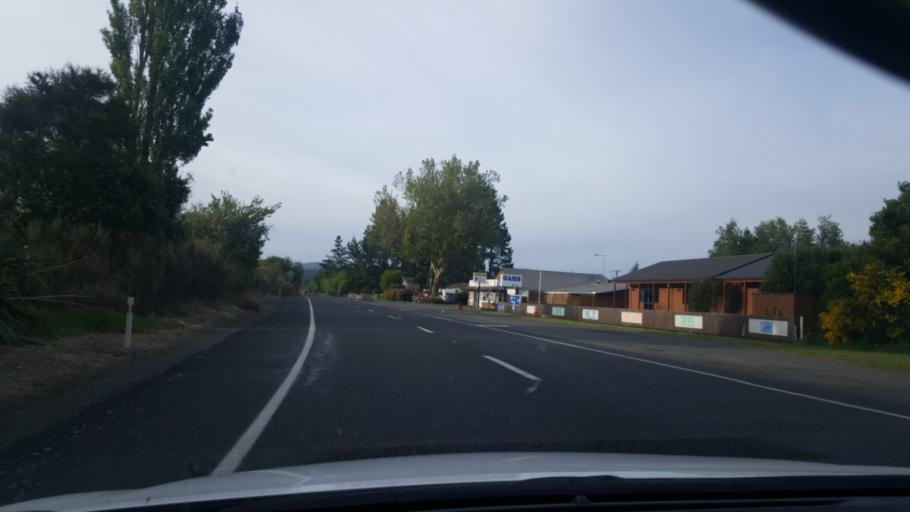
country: NZ
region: Waikato
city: Turangi
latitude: -38.9720
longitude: 175.7704
